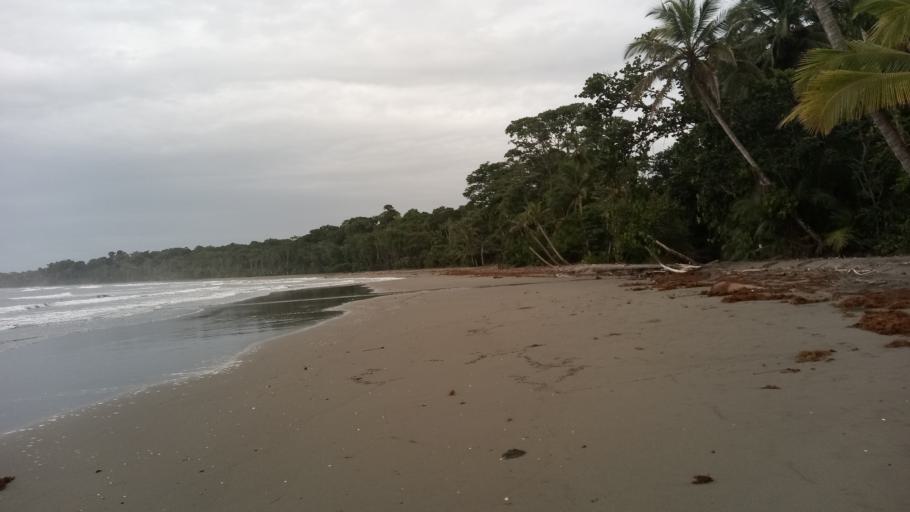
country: CR
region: Limon
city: Sixaola
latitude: 9.6195
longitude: -82.6206
